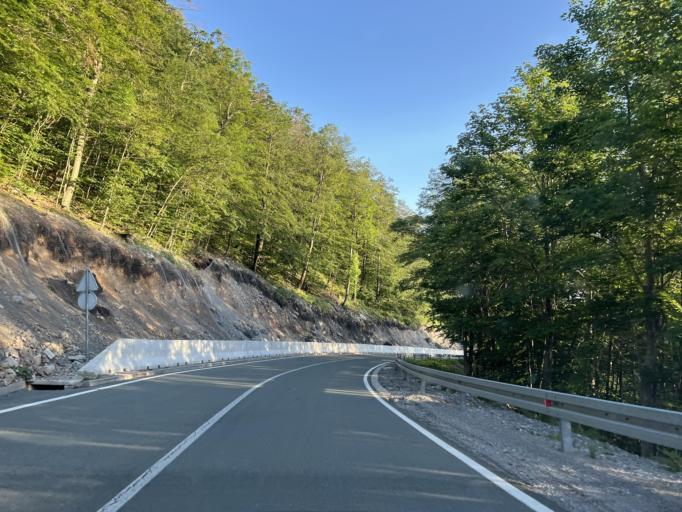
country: HR
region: Primorsko-Goranska
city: Podhum
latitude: 45.4128
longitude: 14.5559
